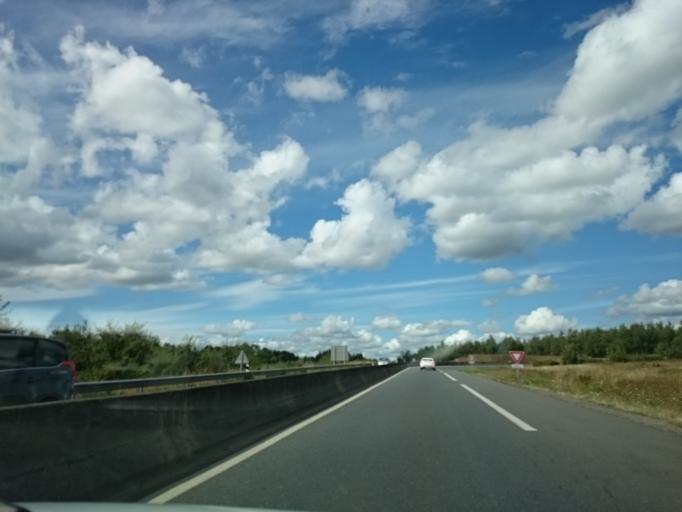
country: FR
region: Pays de la Loire
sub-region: Departement de la Loire-Atlantique
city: Sainte-Luce-sur-Loire
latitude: 47.2365
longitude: -1.4830
